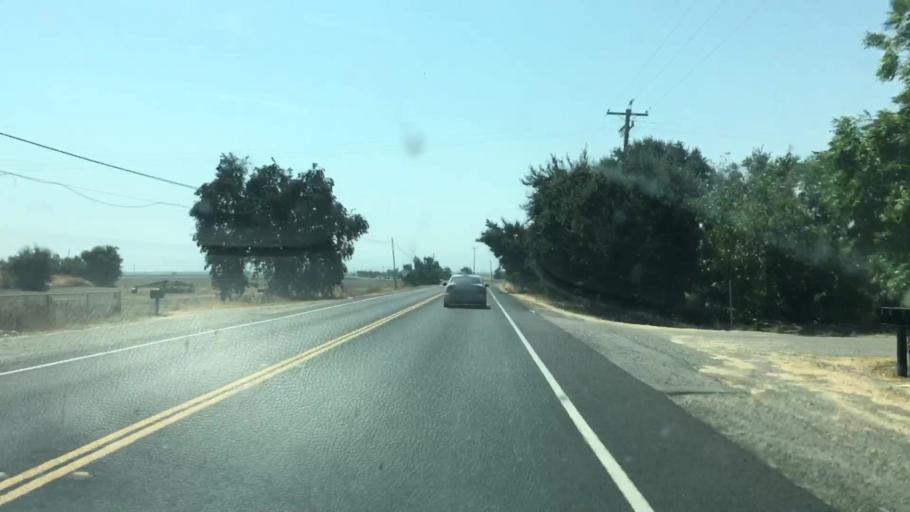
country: US
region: California
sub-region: San Joaquin County
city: Tracy
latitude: 37.8029
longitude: -121.4497
